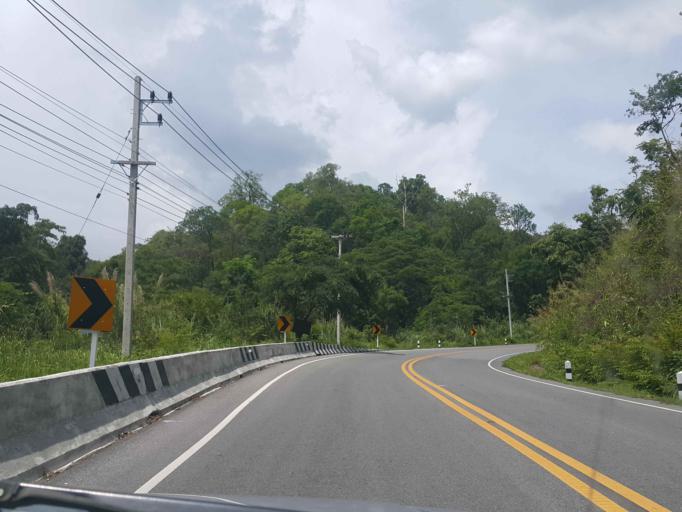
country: TH
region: Nan
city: Ban Luang
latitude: 18.8716
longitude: 100.4788
